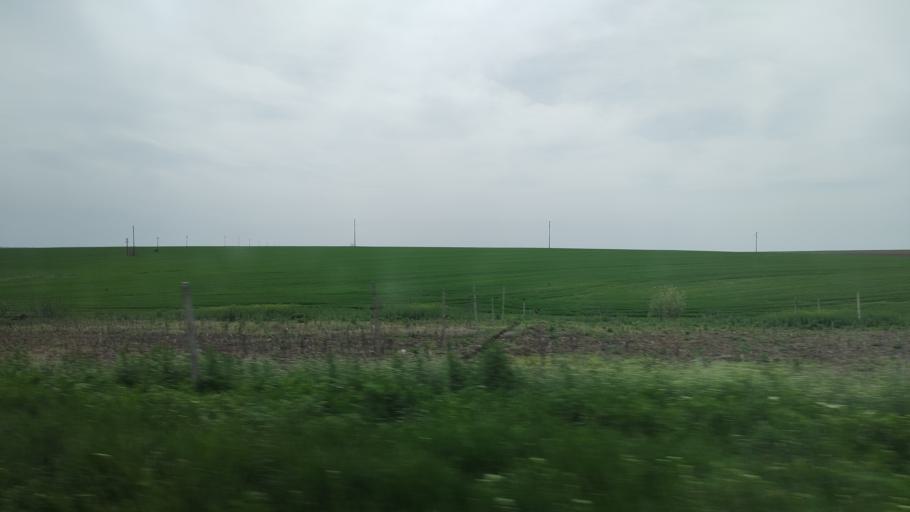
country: RO
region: Constanta
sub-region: Comuna Deleni
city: Pietreni
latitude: 44.0890
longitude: 28.0932
